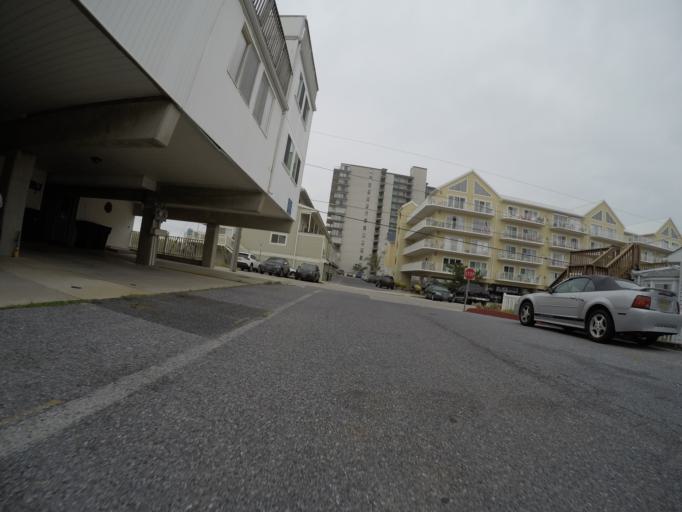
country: US
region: Maryland
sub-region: Worcester County
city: Ocean City
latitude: 38.4063
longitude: -75.0581
